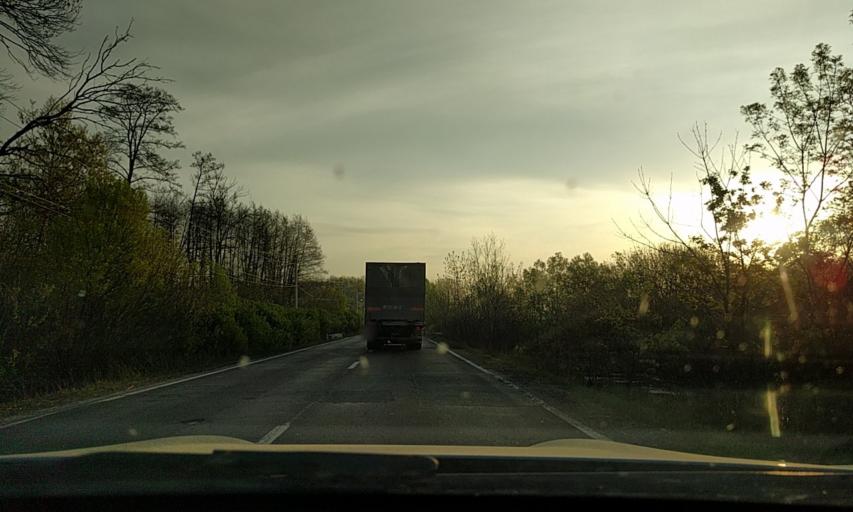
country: RO
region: Brasov
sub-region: Comuna Prejmer
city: Prejmer
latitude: 45.7295
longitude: 25.7364
